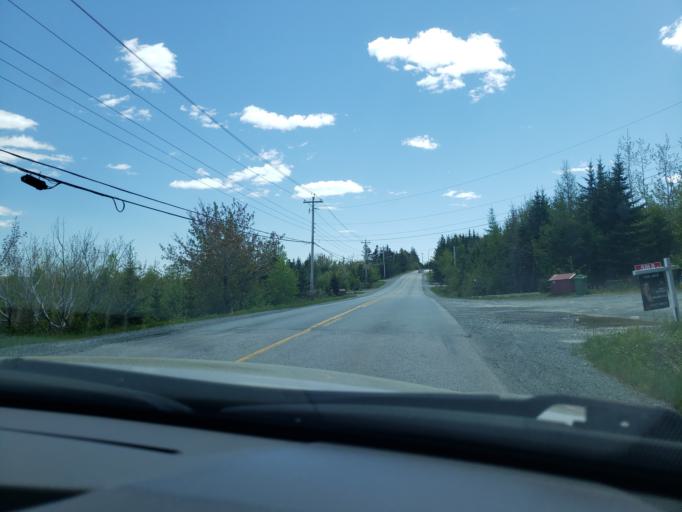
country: CA
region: Nova Scotia
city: Cole Harbour
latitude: 44.7291
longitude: -63.3068
